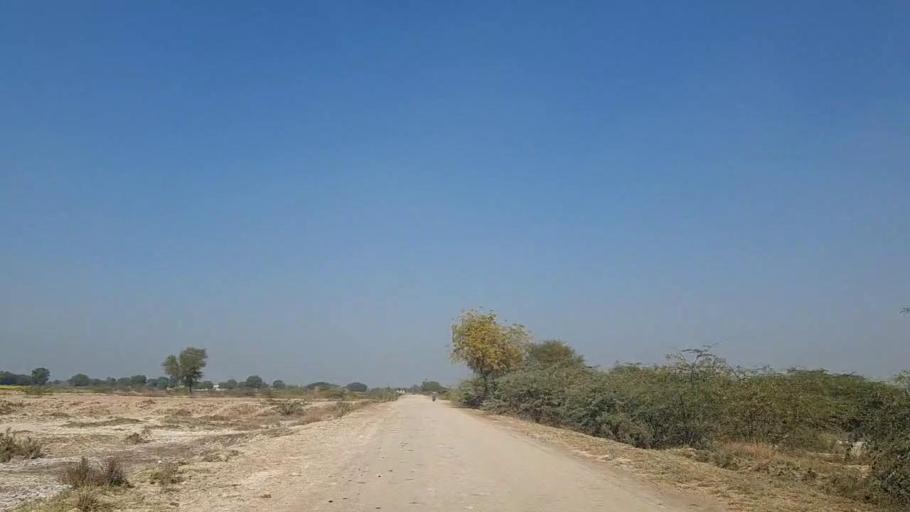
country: PK
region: Sindh
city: Nawabshah
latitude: 26.2219
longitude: 68.3379
